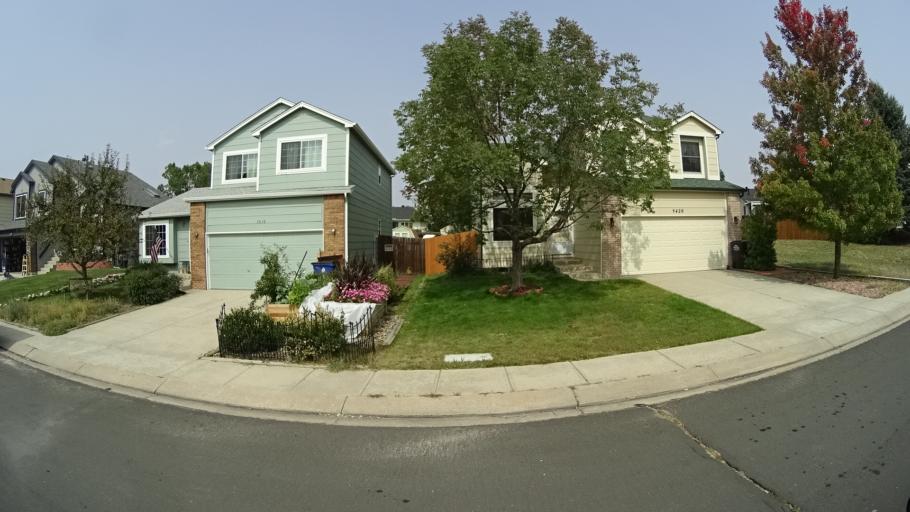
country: US
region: Colorado
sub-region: El Paso County
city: Cimarron Hills
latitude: 38.9216
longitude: -104.7226
